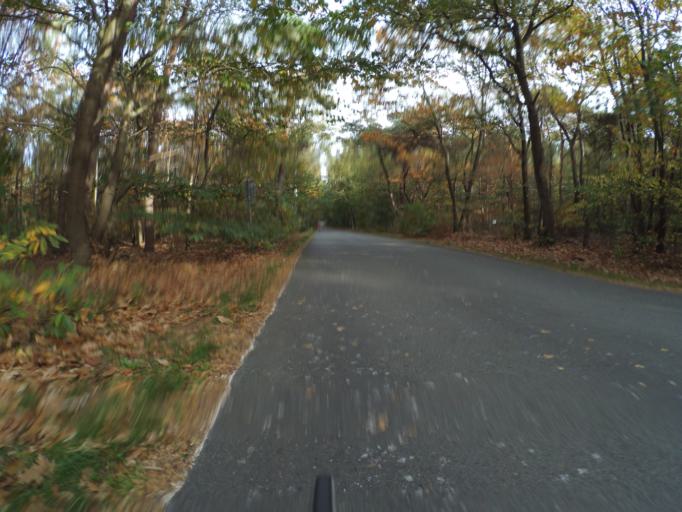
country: NL
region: Overijssel
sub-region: Gemeente Twenterand
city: Den Ham
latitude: 52.3569
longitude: 6.4360
